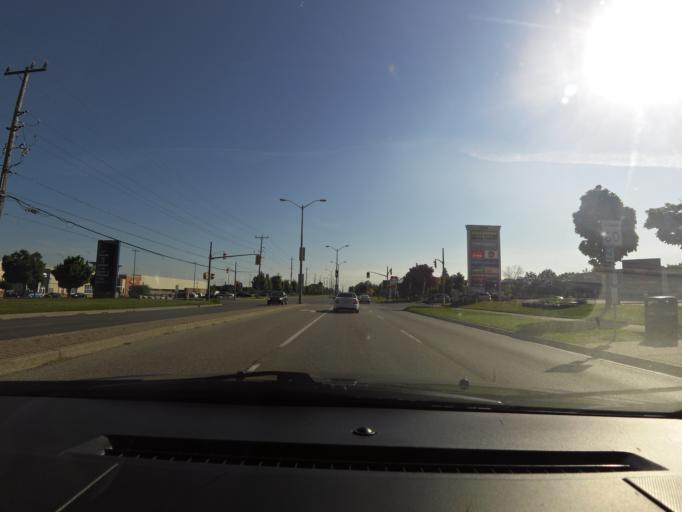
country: CA
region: Ontario
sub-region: Wellington County
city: Guelph
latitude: 43.5175
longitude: -80.2369
